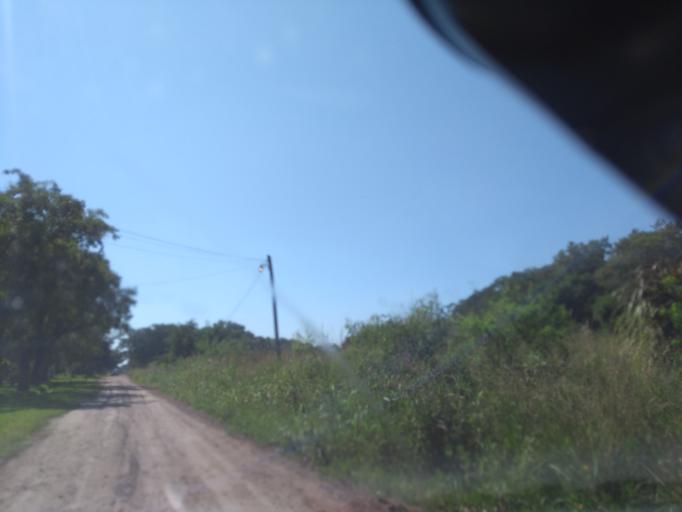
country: AR
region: Chaco
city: Resistencia
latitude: -27.4347
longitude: -58.9444
